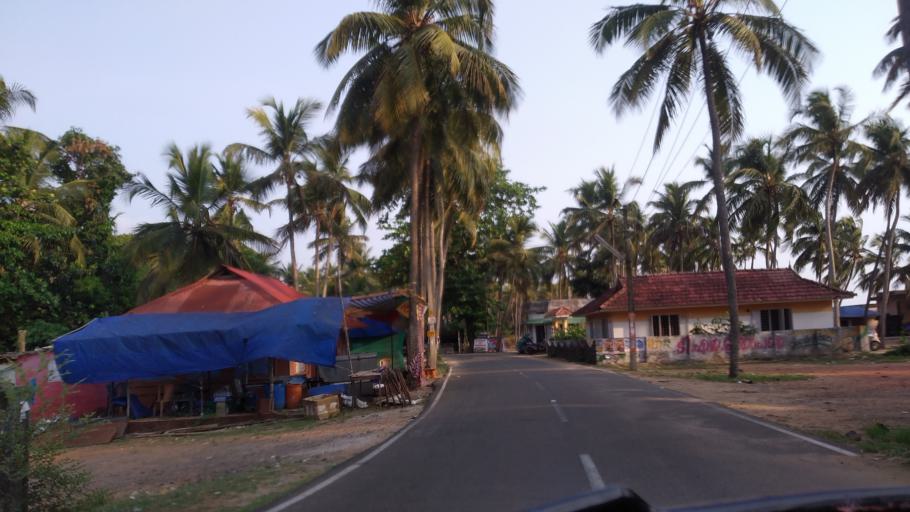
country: IN
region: Kerala
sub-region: Thrissur District
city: Thanniyam
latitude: 10.4318
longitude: 76.0781
